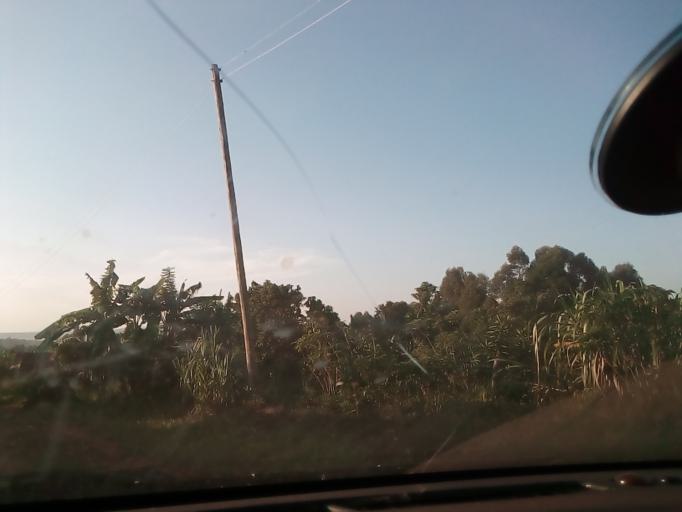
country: UG
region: Central Region
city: Masaka
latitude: -0.3399
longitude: 31.7574
